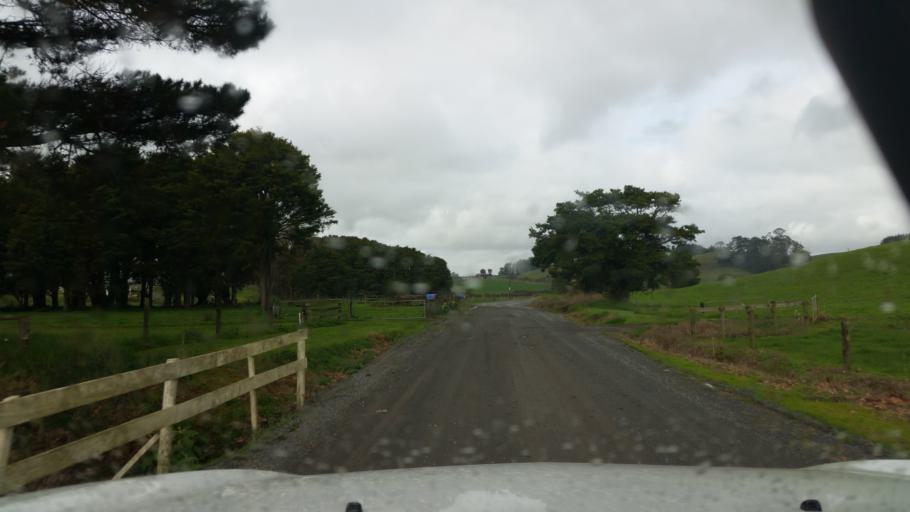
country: NZ
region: Northland
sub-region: Whangarei
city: Maungatapere
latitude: -35.6117
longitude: 174.1852
